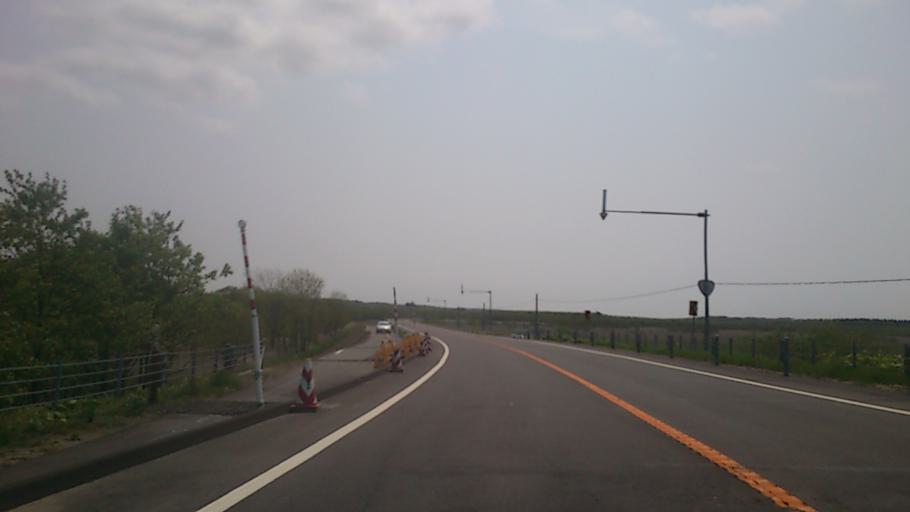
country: JP
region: Hokkaido
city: Nemuro
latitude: 43.2761
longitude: 145.2300
